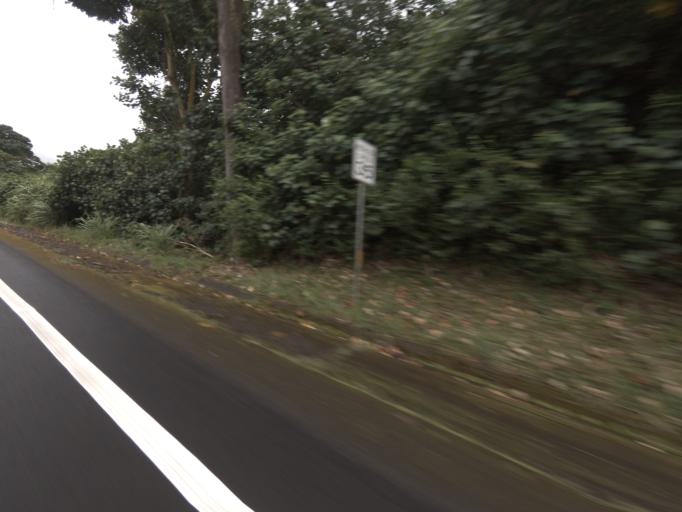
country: US
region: Hawaii
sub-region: Honolulu County
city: Kane'ohe
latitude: 21.3818
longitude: -157.8132
